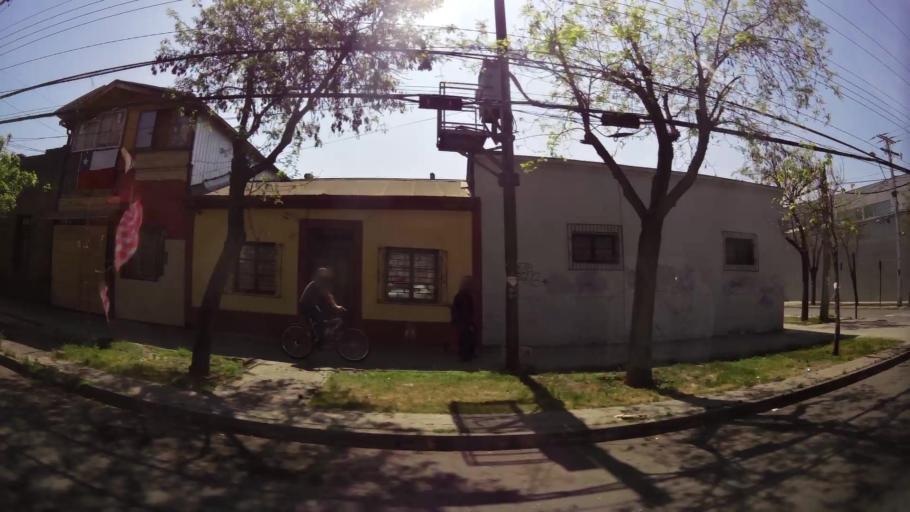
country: CL
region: Santiago Metropolitan
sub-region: Provincia de Santiago
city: Santiago
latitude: -33.4665
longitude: -70.6416
